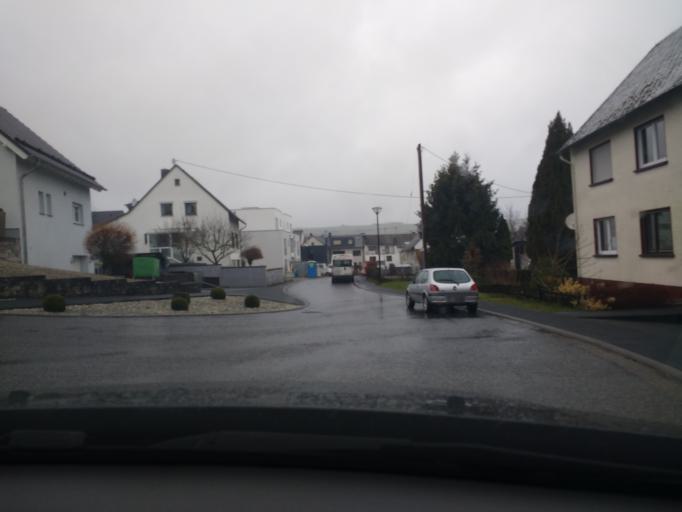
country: DE
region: Rheinland-Pfalz
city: Pluwig
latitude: 49.6885
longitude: 6.7210
